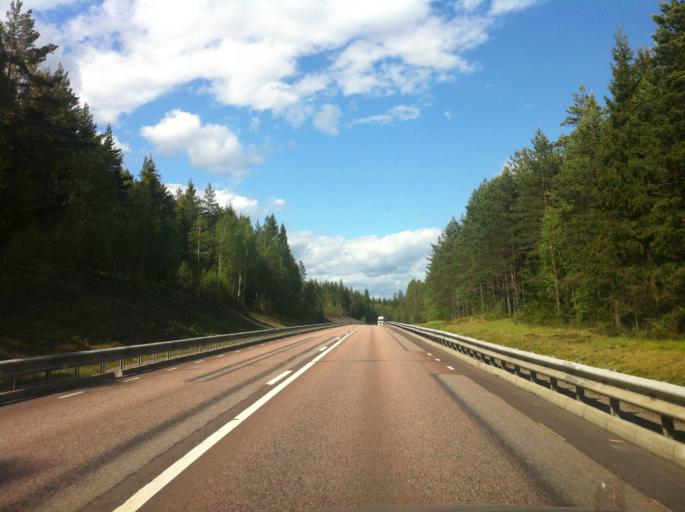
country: SE
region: Vaermland
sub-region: Kristinehamns Kommun
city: Kristinehamn
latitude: 59.3765
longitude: 14.1727
